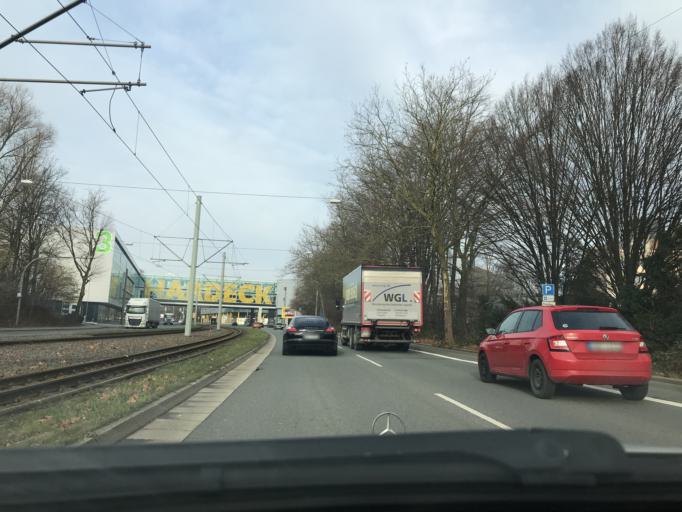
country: DE
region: North Rhine-Westphalia
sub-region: Regierungsbezirk Arnsberg
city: Bochum
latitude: 51.4702
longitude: 7.2671
